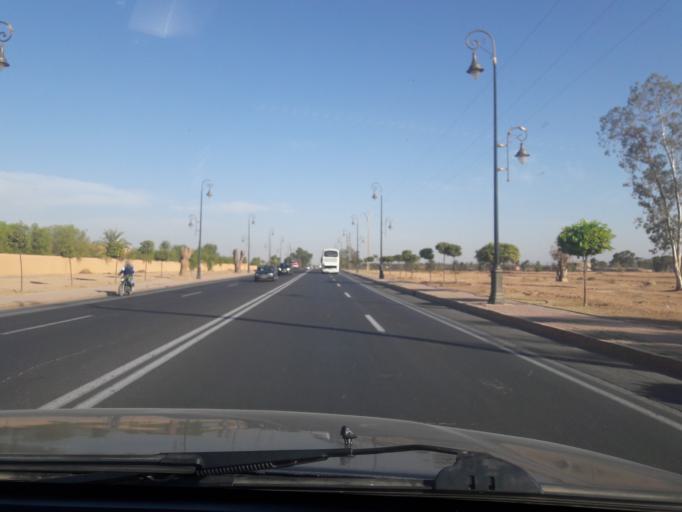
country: MA
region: Marrakech-Tensift-Al Haouz
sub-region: Marrakech
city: Marrakesh
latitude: 31.6480
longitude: -7.9383
